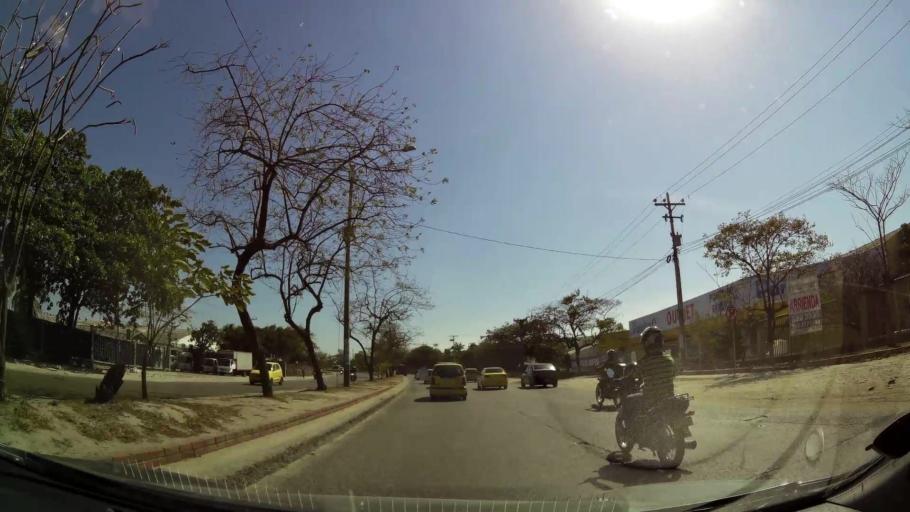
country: CO
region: Atlantico
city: Barranquilla
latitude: 10.9549
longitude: -74.7866
